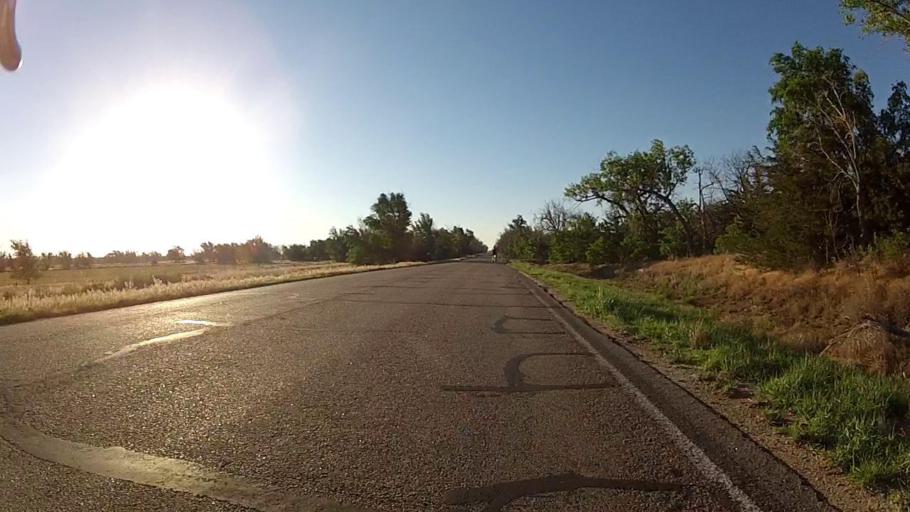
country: US
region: Kansas
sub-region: Ford County
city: Dodge City
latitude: 37.7140
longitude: -99.9298
